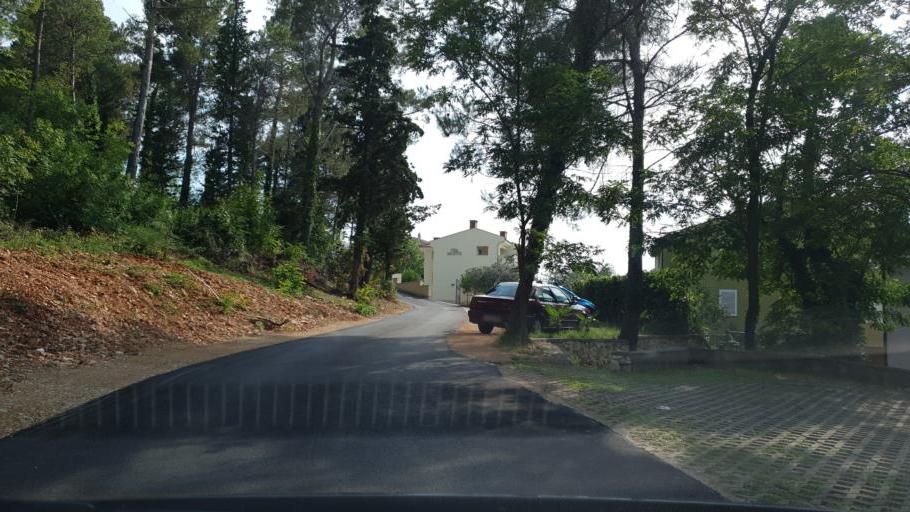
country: HR
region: Primorsko-Goranska
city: Njivice
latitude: 45.1497
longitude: 14.6089
